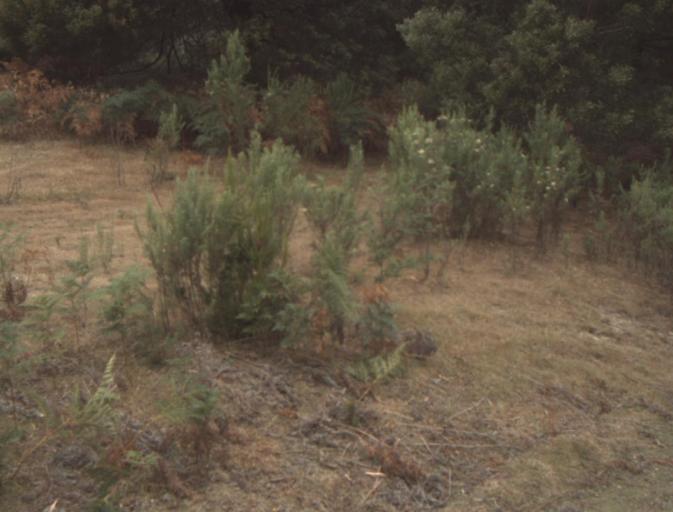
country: AU
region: Tasmania
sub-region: Launceston
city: Mayfield
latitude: -41.1561
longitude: 147.1729
